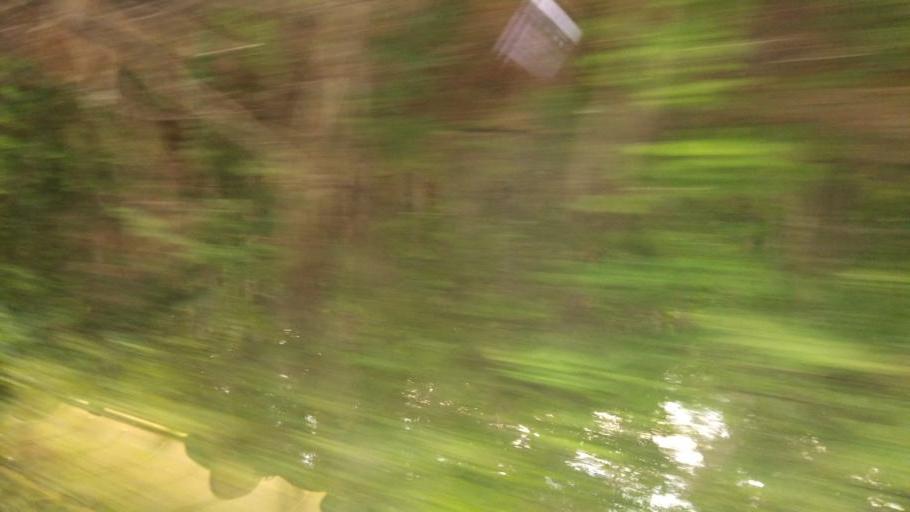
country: US
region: Virginia
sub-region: Culpeper County
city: Culpeper
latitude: 38.4839
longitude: -77.9549
